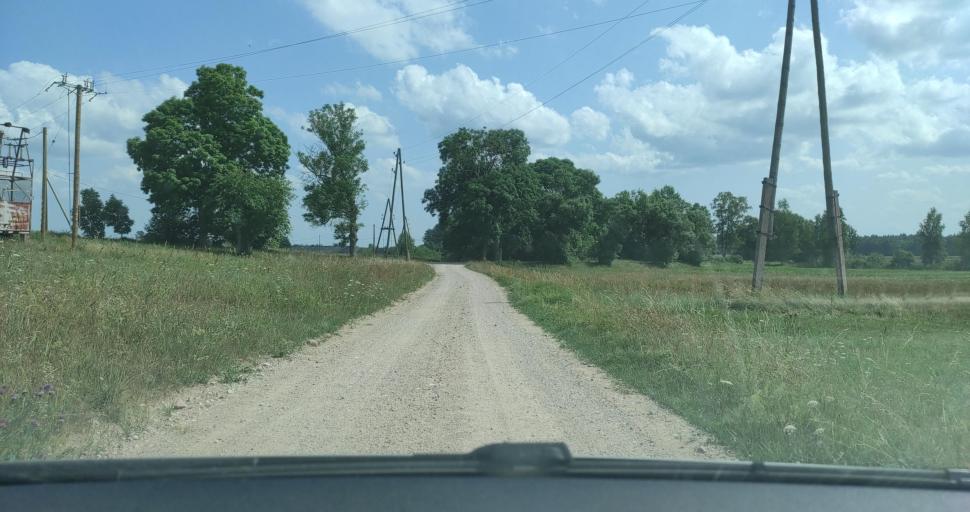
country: LV
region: Kuldigas Rajons
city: Kuldiga
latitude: 57.0643
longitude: 22.2444
